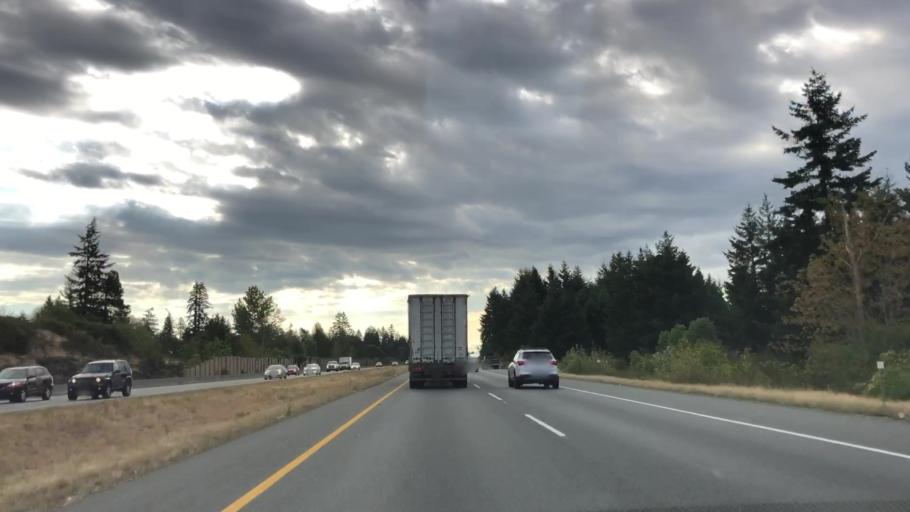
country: CA
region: British Columbia
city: Nanaimo
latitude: 49.1940
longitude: -124.0184
